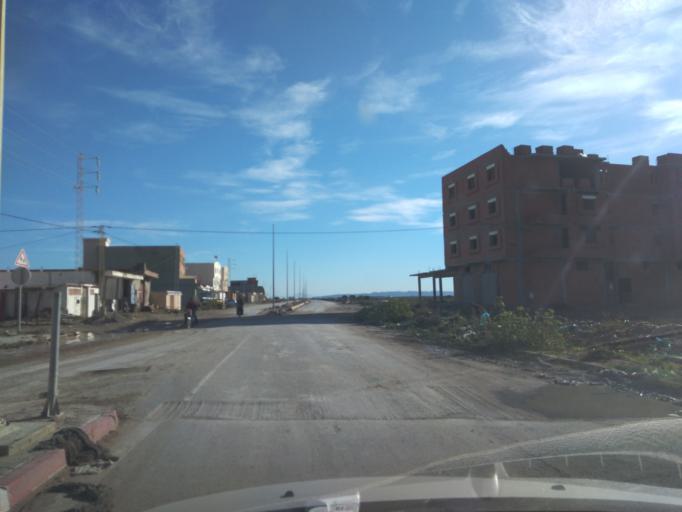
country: TN
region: Ariana
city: Qal'at al Andalus
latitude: 37.0527
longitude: 10.1223
